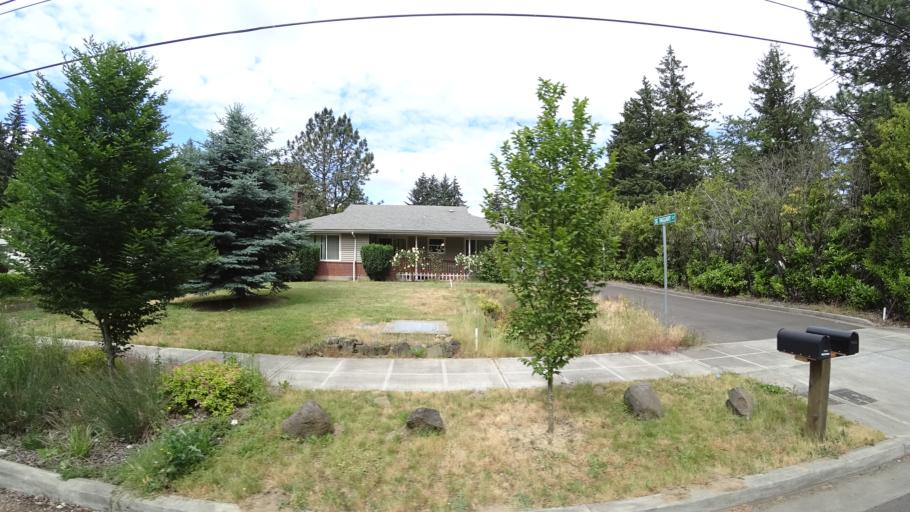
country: US
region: Oregon
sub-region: Multnomah County
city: Lents
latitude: 45.5016
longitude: -122.5262
